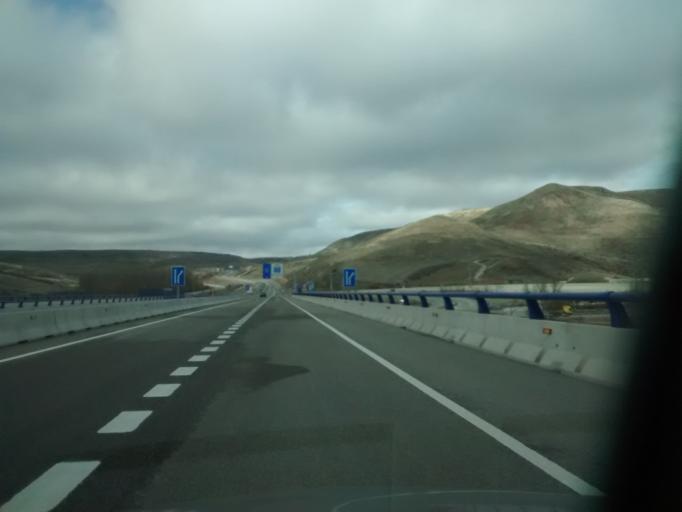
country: ES
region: Castille and Leon
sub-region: Provincia de Soria
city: Medinaceli
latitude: 41.1693
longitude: -2.4183
